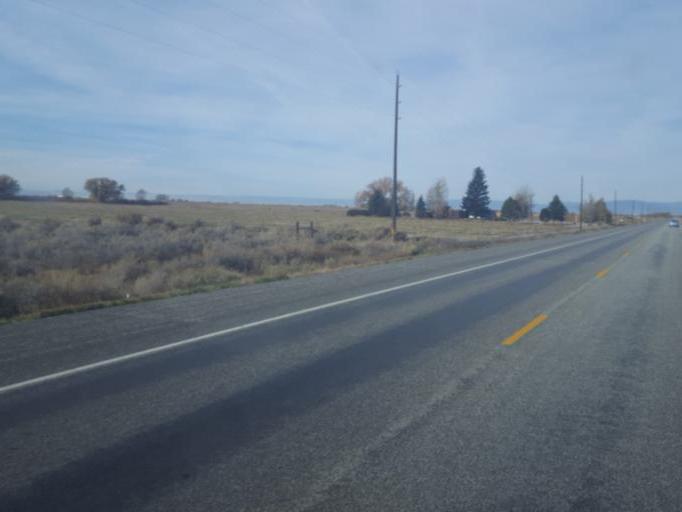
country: US
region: Colorado
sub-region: Alamosa County
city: Alamosa East
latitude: 37.4741
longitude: -105.7528
